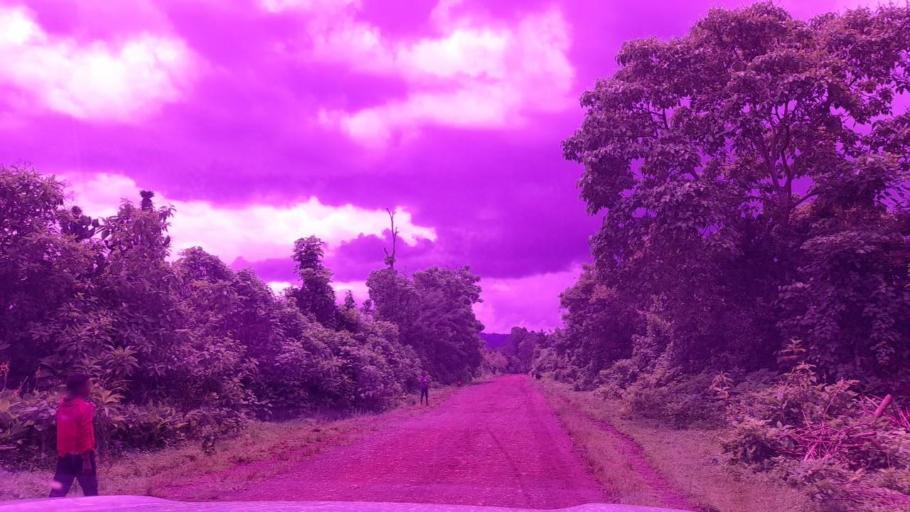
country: ET
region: Southern Nations, Nationalities, and People's Region
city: Tippi
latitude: 7.6281
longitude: 35.5800
